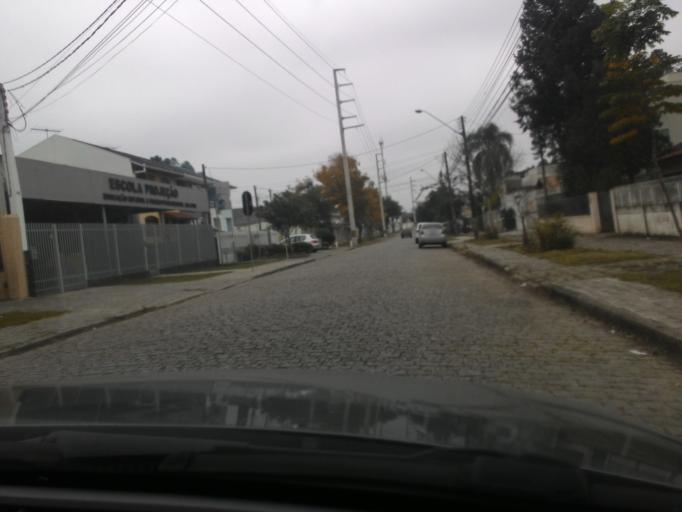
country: BR
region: Parana
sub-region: Curitiba
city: Curitiba
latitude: -25.4614
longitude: -49.2455
